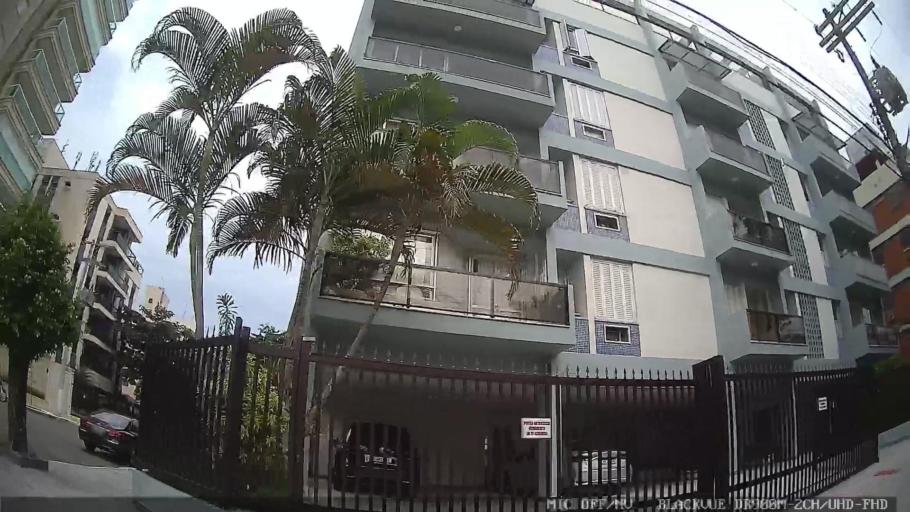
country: BR
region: Sao Paulo
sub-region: Guaruja
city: Guaruja
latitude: -23.9825
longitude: -46.2265
